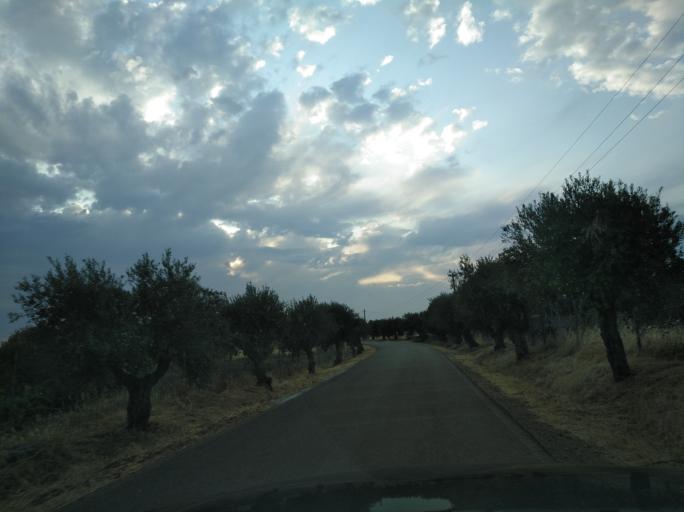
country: PT
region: Portalegre
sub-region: Campo Maior
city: Campo Maior
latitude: 39.0168
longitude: -7.0460
